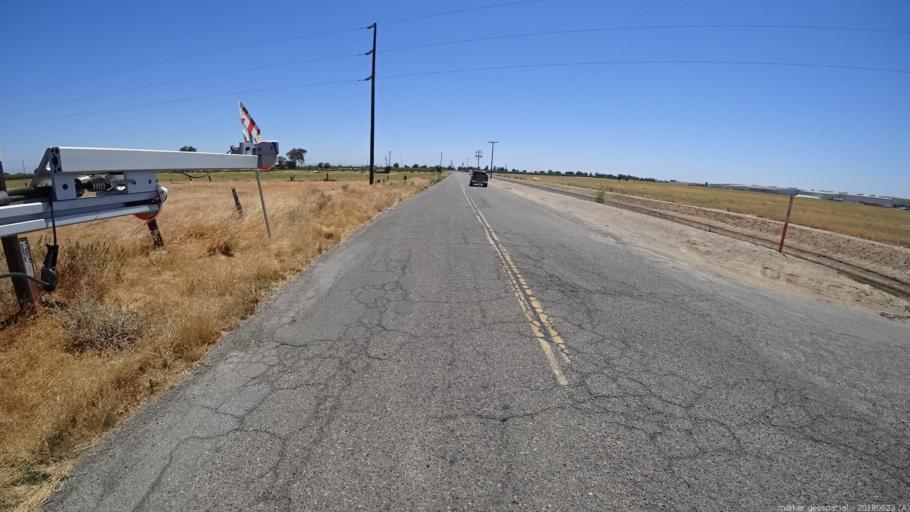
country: US
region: California
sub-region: Madera County
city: Chowchilla
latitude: 37.0982
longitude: -120.2294
